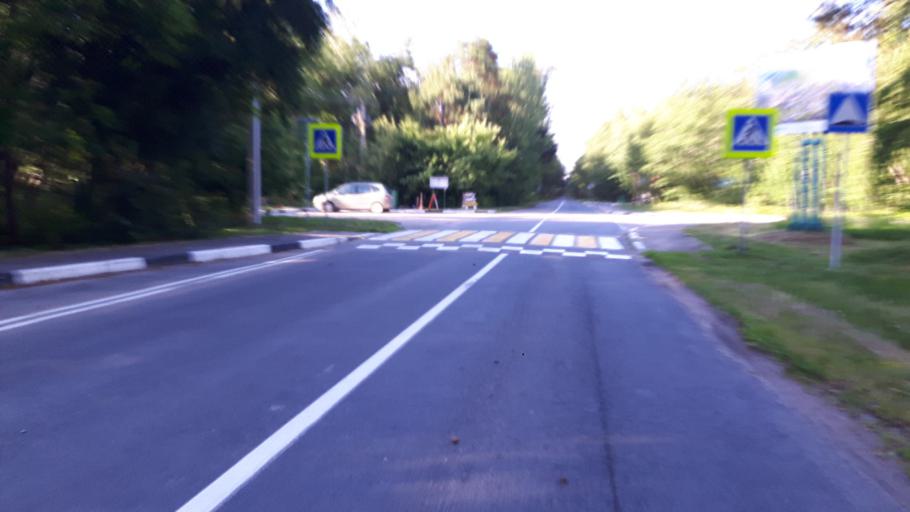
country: LT
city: Nida
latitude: 55.2368
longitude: 20.9096
